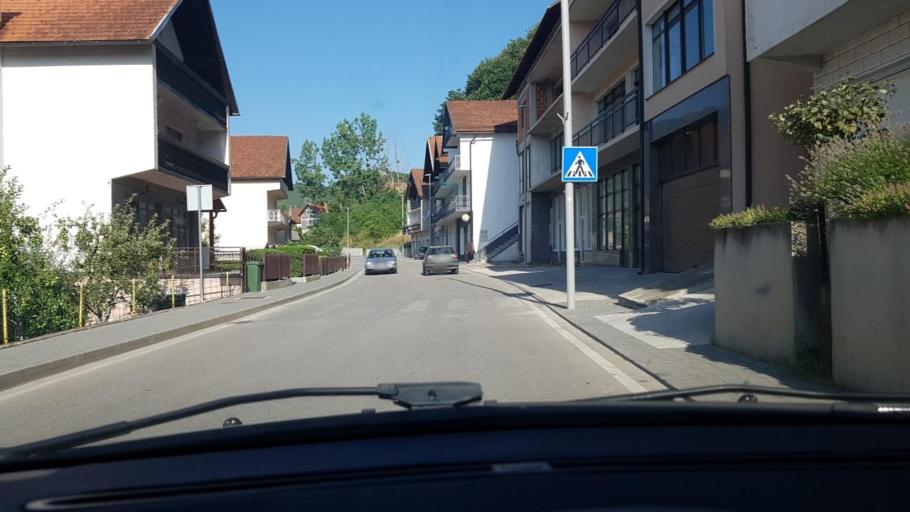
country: BA
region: Federation of Bosnia and Herzegovina
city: Prozor
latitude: 43.8233
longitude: 17.6055
